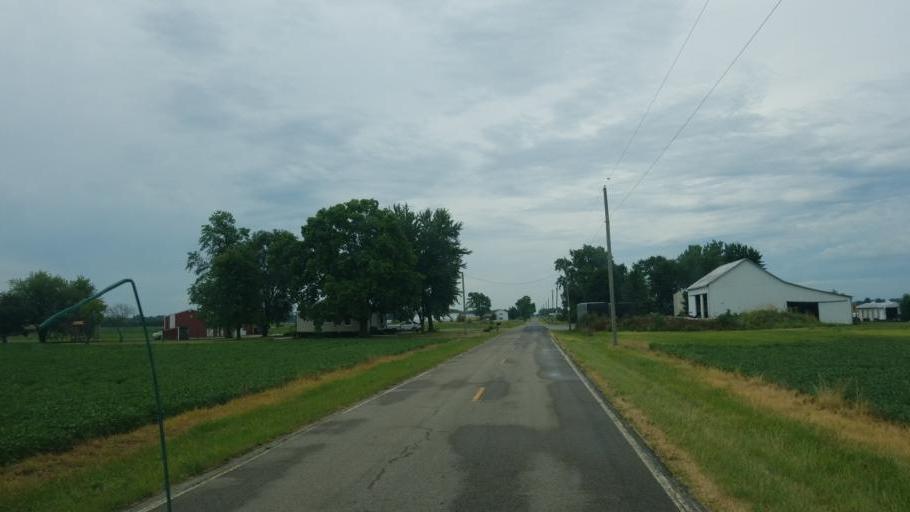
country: US
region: Ohio
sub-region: Defiance County
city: Hicksville
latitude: 41.2769
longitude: -84.6895
